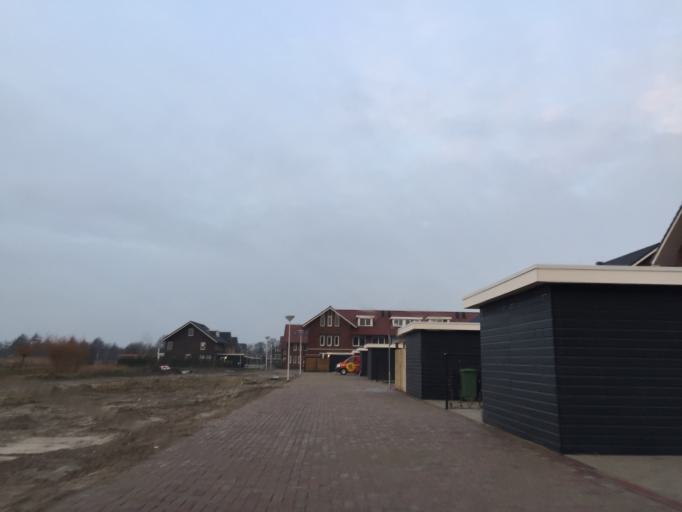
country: NL
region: South Holland
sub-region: Gemeente Pijnacker-Nootdorp
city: Pijnacker
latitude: 52.0045
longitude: 4.4403
